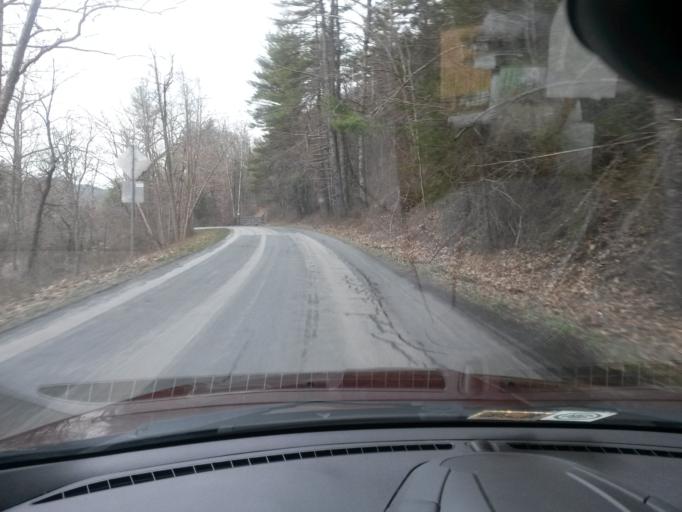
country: US
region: Virginia
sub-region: Bath County
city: Warm Springs
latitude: 38.0377
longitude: -79.8573
